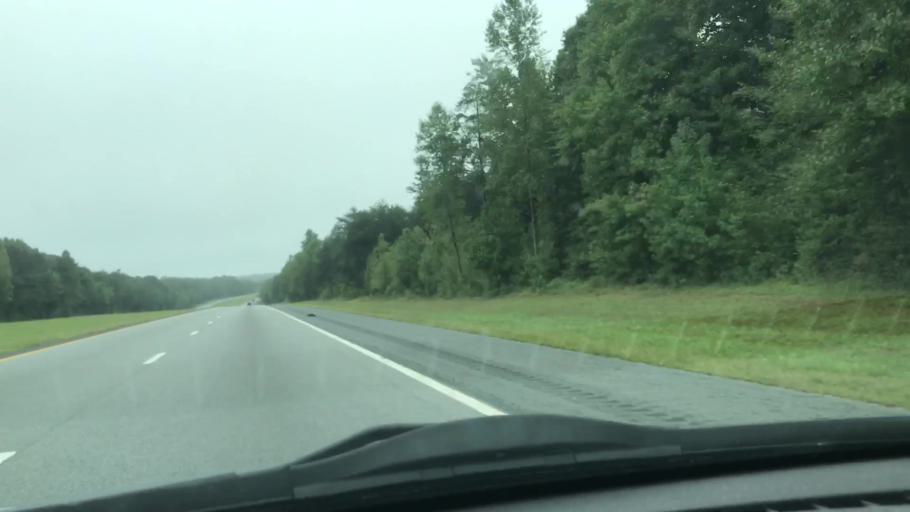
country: US
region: North Carolina
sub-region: Guilford County
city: Pleasant Garden
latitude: 35.9649
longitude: -79.8209
